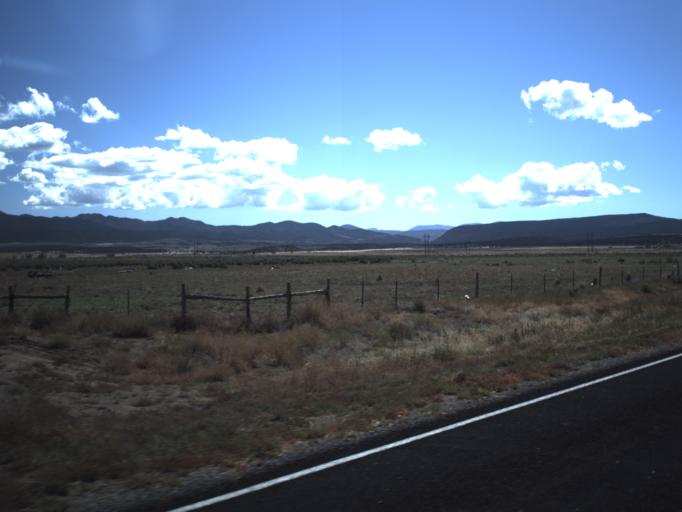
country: US
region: Utah
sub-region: Washington County
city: Enterprise
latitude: 37.6173
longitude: -113.6612
